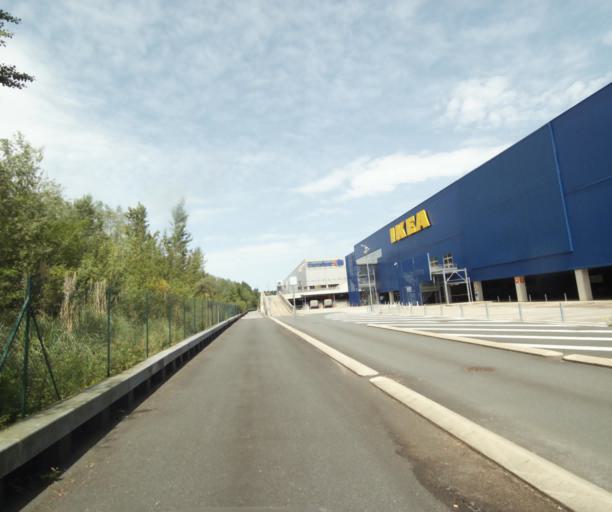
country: FR
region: Aquitaine
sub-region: Departement des Pyrenees-Atlantiques
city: Mouguerre
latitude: 43.4789
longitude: -1.4461
